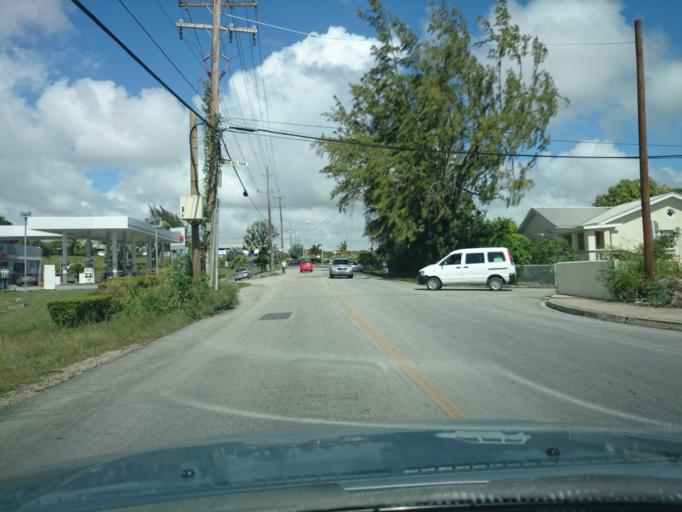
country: BB
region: Christ Church
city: Oistins
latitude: 13.0773
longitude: -59.5583
